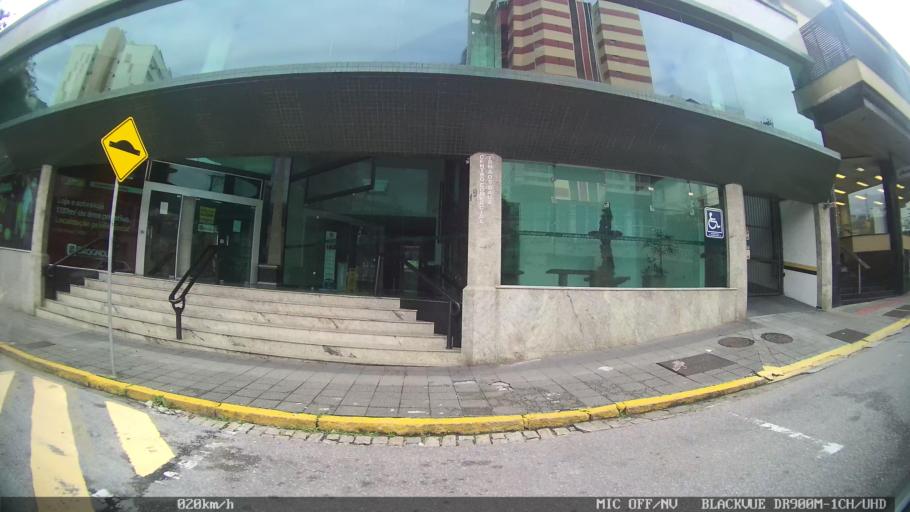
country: BR
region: Santa Catarina
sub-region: Florianopolis
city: Florianopolis
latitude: -27.5946
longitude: -48.5504
